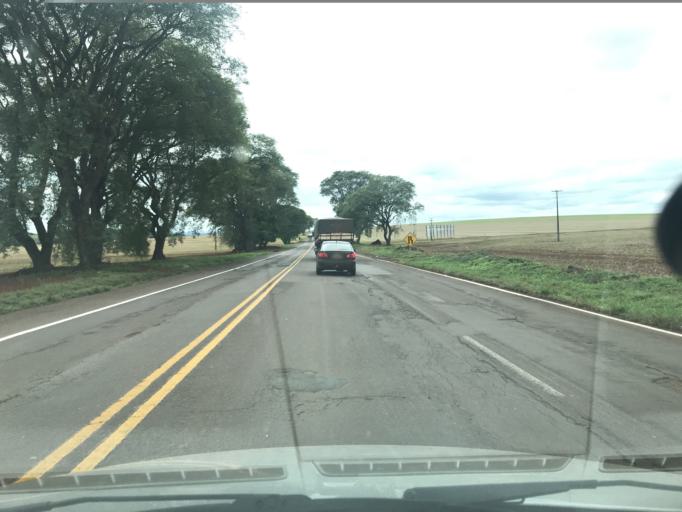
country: BR
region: Parana
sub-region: Terra Boa
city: Terra Boa
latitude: -23.6096
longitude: -52.4211
